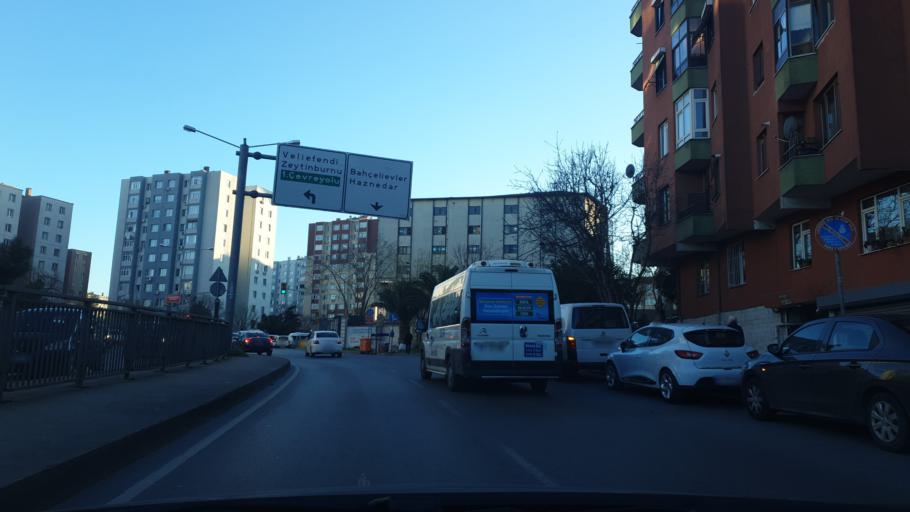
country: TR
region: Istanbul
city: merter keresteciler
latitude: 41.0095
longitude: 28.8752
